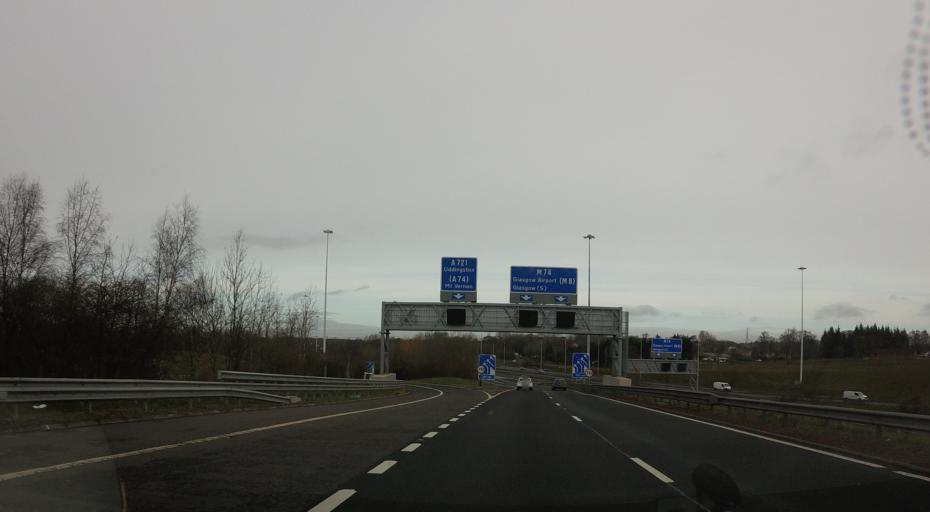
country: GB
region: Scotland
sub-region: South Lanarkshire
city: Uddingston
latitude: 55.8331
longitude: -4.1037
